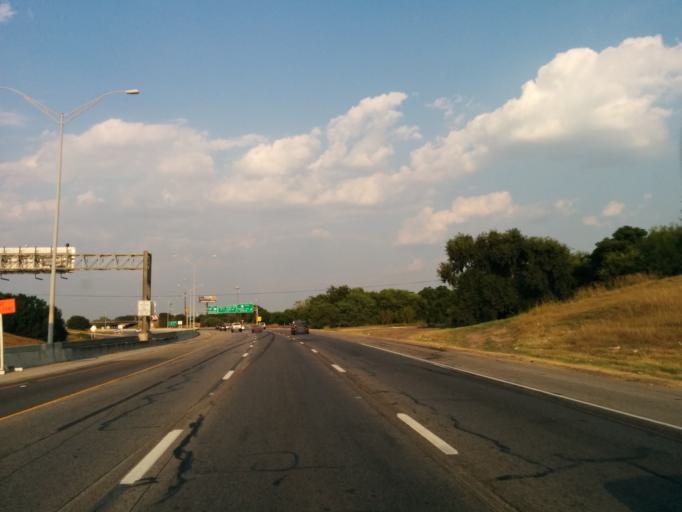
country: US
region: Texas
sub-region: Bexar County
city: San Antonio
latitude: 29.4015
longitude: -98.4494
